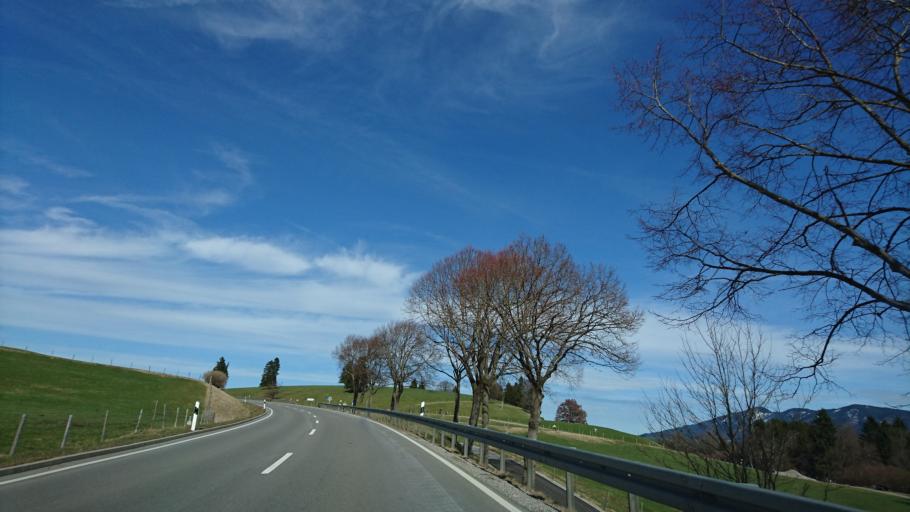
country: DE
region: Bavaria
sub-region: Swabia
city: Rosshaupten
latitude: 47.6236
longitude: 10.7212
